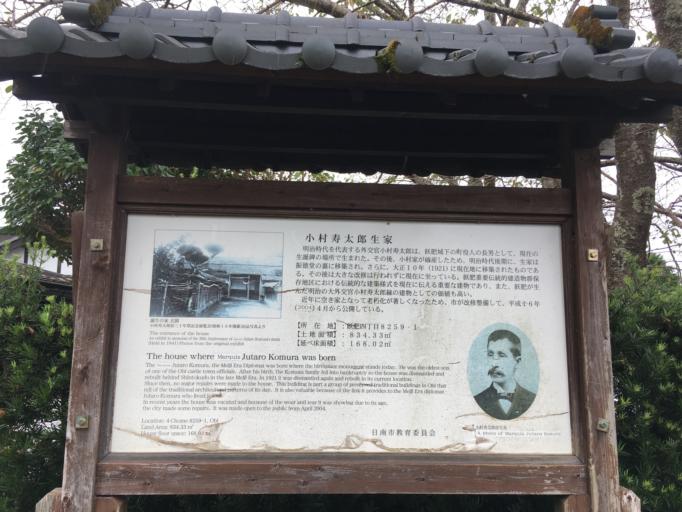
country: JP
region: Miyazaki
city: Nichinan
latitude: 31.6280
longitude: 131.3530
